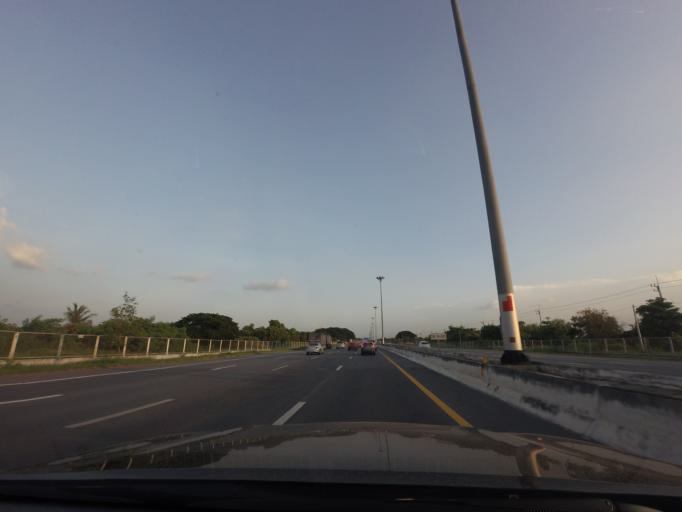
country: TH
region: Pathum Thani
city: Khlong Luang
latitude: 14.1089
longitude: 100.6821
